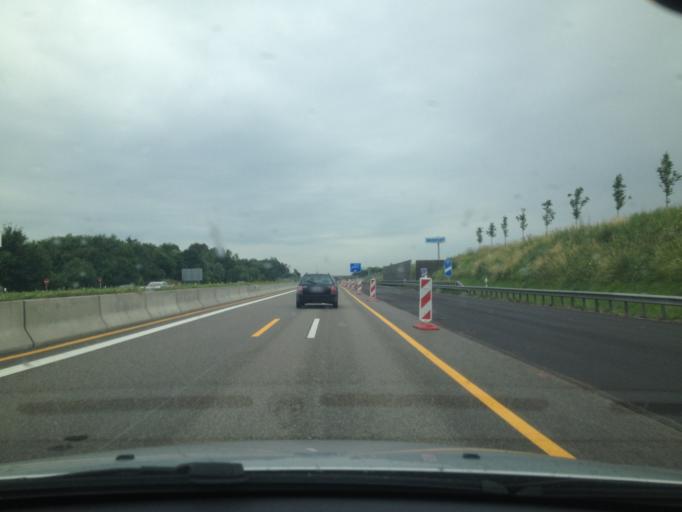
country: DE
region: Bavaria
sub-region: Swabia
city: Leipheim
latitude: 48.4396
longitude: 10.2134
